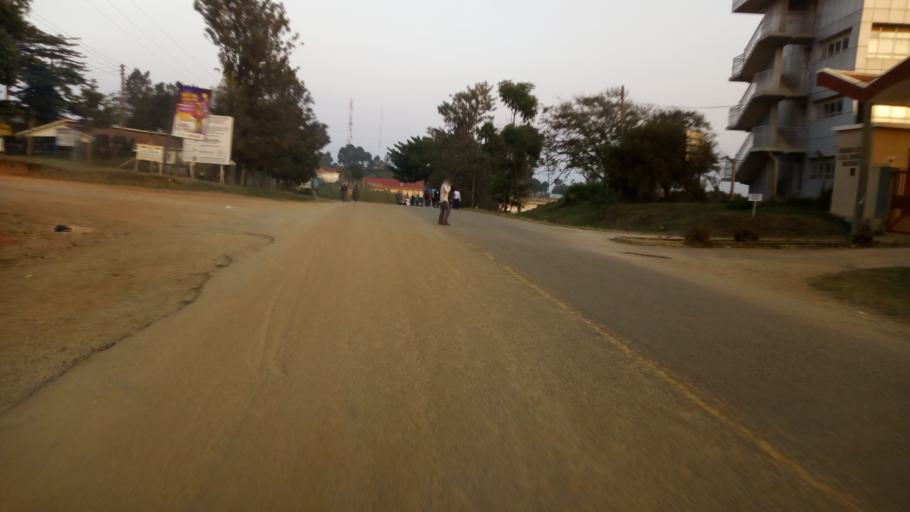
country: UG
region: Western Region
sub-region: Rukungiri District
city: Rukungiri
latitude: -0.7839
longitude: 29.9259
